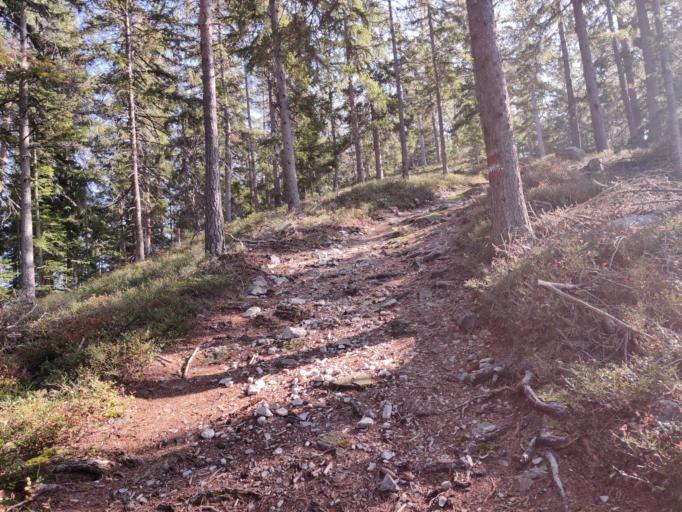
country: AT
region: Styria
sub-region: Politischer Bezirk Hartberg-Fuerstenfeld
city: Sankt Jakob im Walde
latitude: 47.4684
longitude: 15.8161
